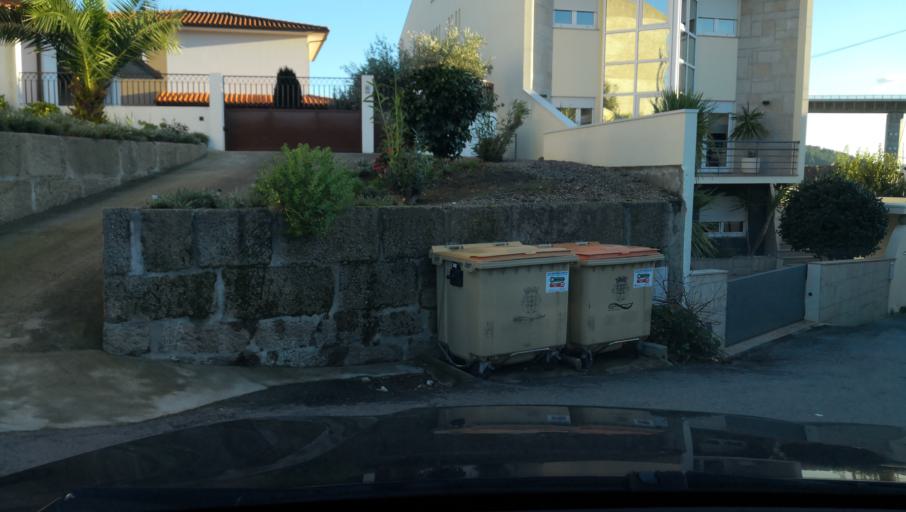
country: PT
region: Vila Real
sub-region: Vila Real
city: Vila Real
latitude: 41.2803
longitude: -7.7411
